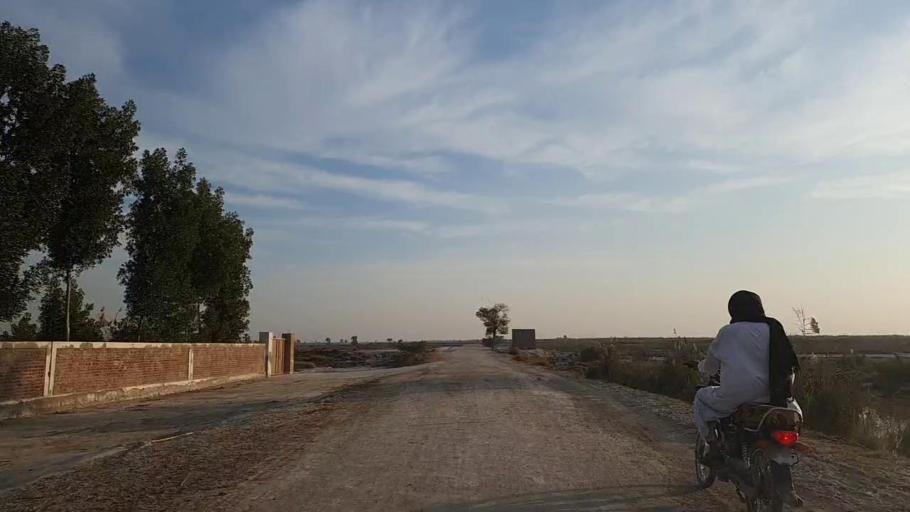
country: PK
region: Sindh
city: Bandhi
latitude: 26.5827
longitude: 68.3334
